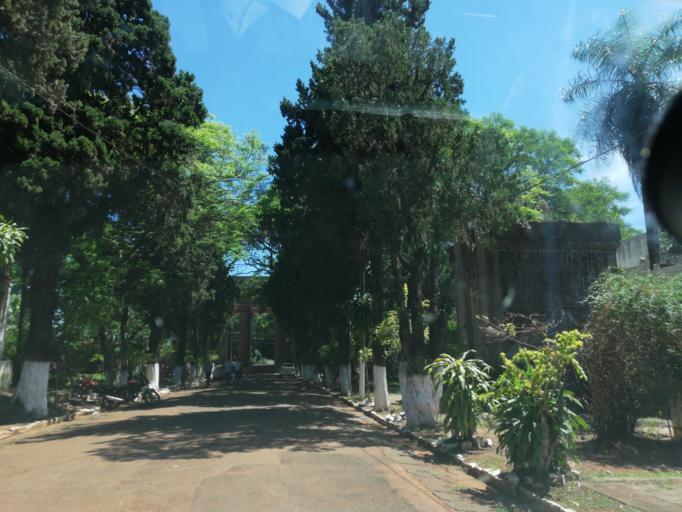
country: AR
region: Misiones
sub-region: Departamento de Capital
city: Posadas
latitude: -27.3805
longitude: -55.9127
